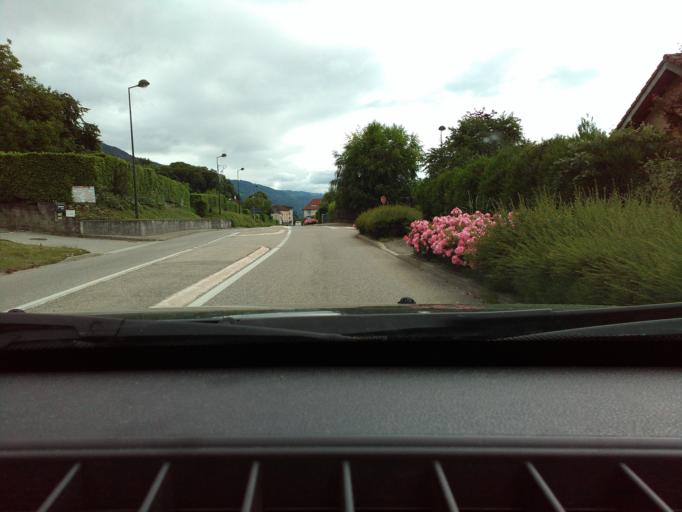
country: FR
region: Rhone-Alpes
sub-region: Departement de l'Isere
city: Goncelin
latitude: 45.3467
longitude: 5.9796
